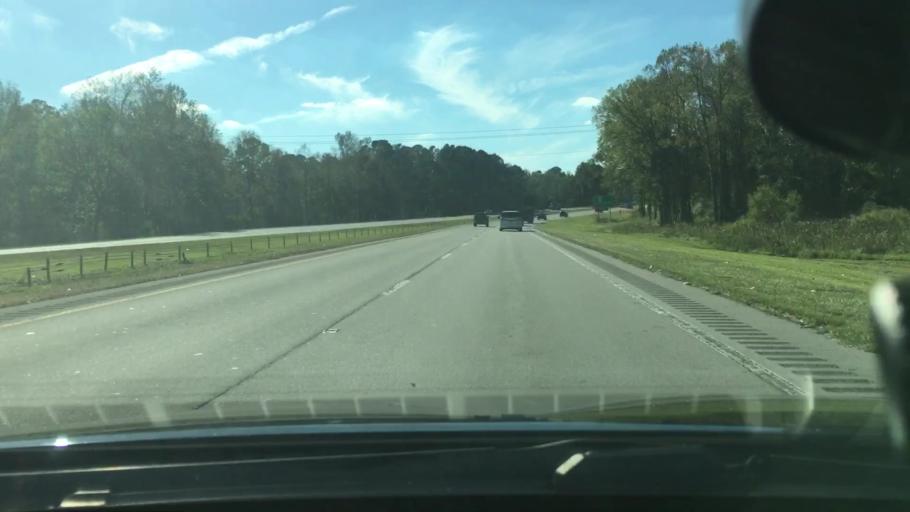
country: US
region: North Carolina
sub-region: Craven County
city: Trent Woods
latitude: 35.1000
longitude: -77.0711
